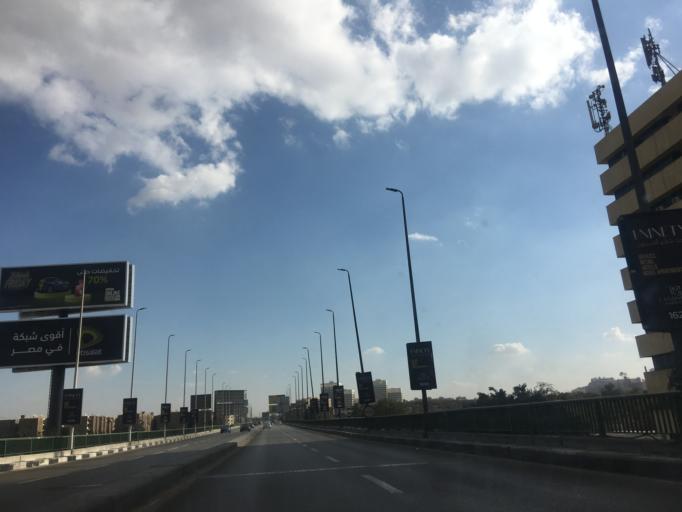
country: EG
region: Muhafazat al Qahirah
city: Cairo
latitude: 30.0669
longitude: 31.2938
